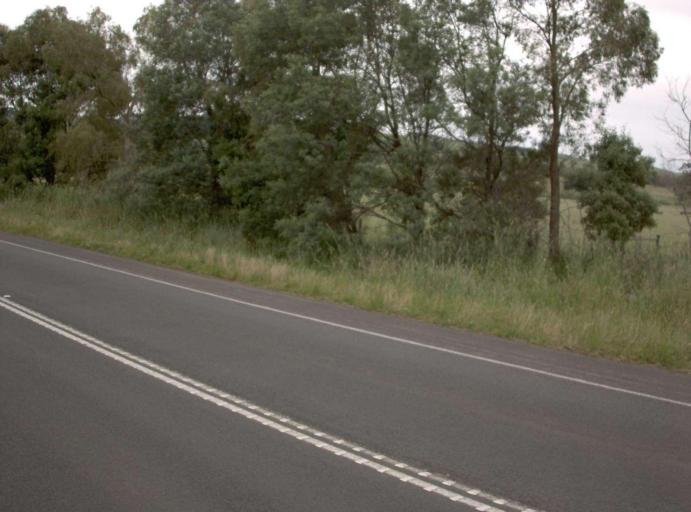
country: AU
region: Victoria
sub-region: Bass Coast
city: North Wonthaggi
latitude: -38.3680
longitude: 145.6668
